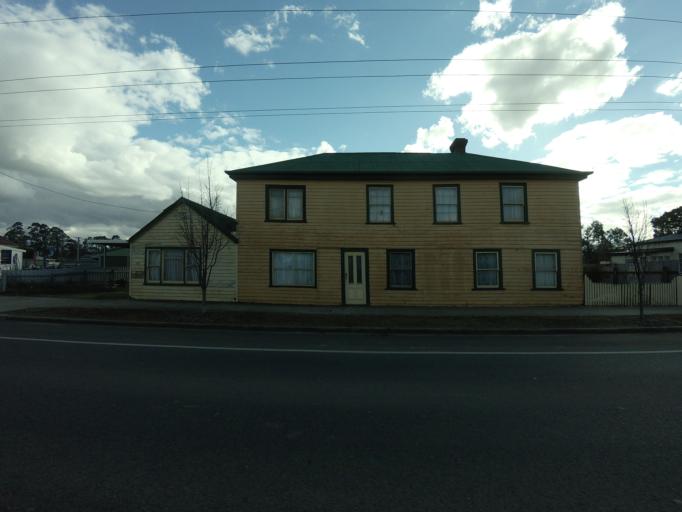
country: AU
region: Tasmania
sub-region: Northern Midlands
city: Longford
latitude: -41.6843
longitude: 147.0807
